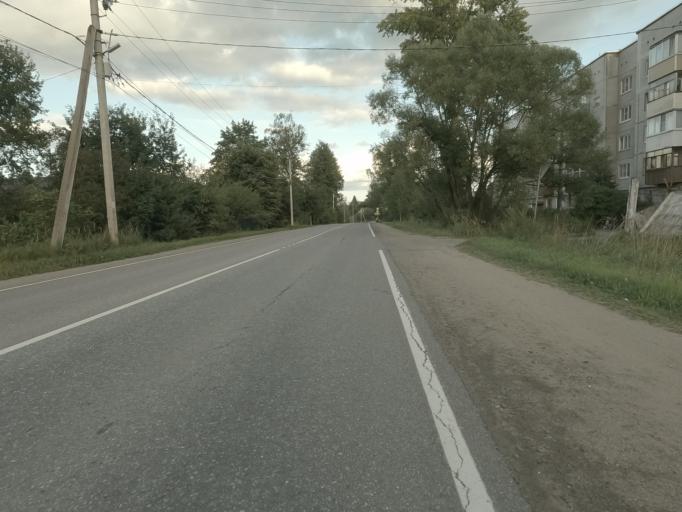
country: RU
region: Leningrad
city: Mga
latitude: 59.7521
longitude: 31.0455
